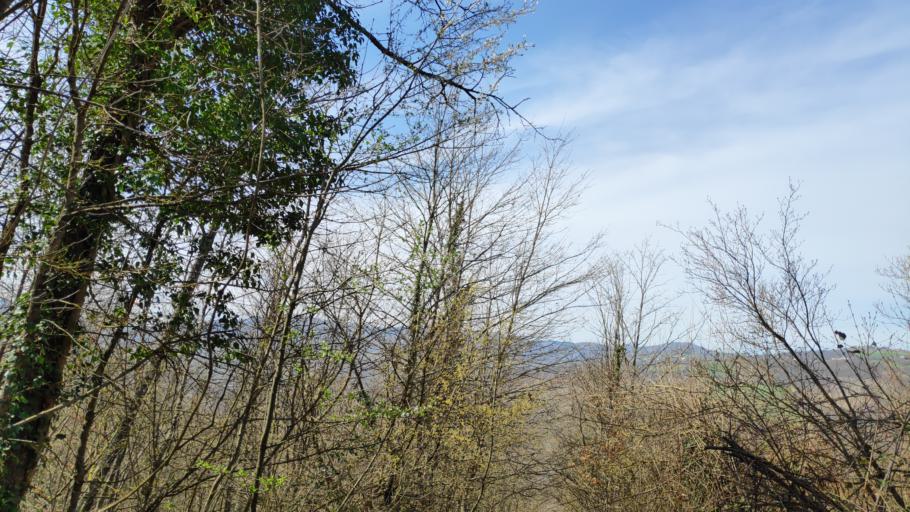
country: IT
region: Emilia-Romagna
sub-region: Provincia di Bologna
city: Berzantina
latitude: 44.1768
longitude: 10.9952
